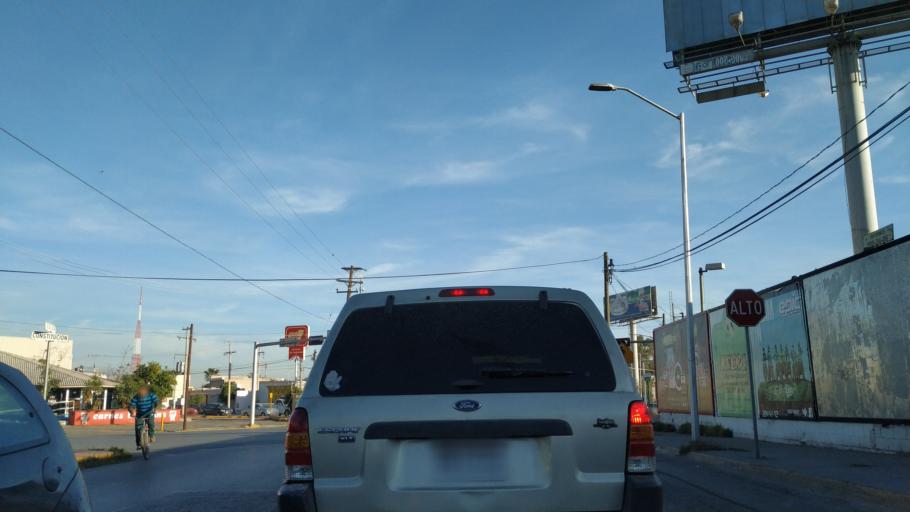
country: MX
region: Coahuila
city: Torreon
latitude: 25.5502
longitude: -103.4486
